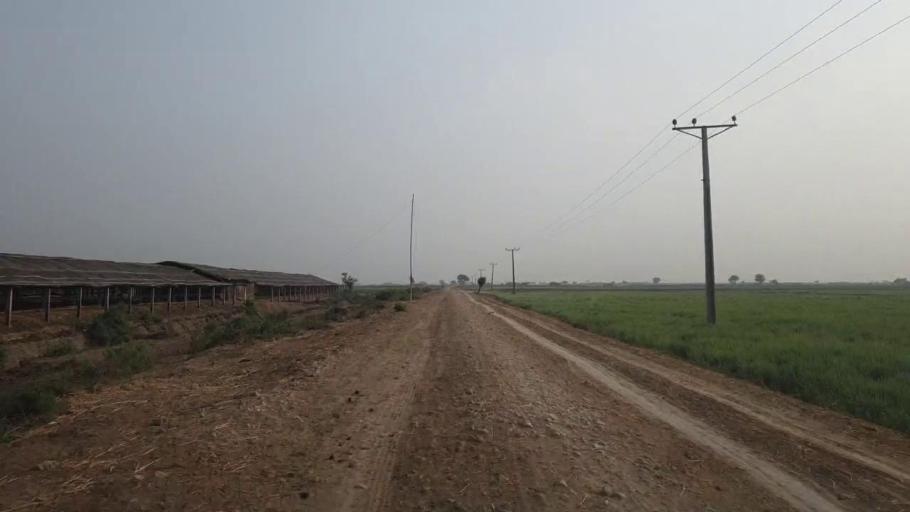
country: PK
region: Sindh
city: Mirpur Batoro
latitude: 24.5516
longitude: 68.4207
